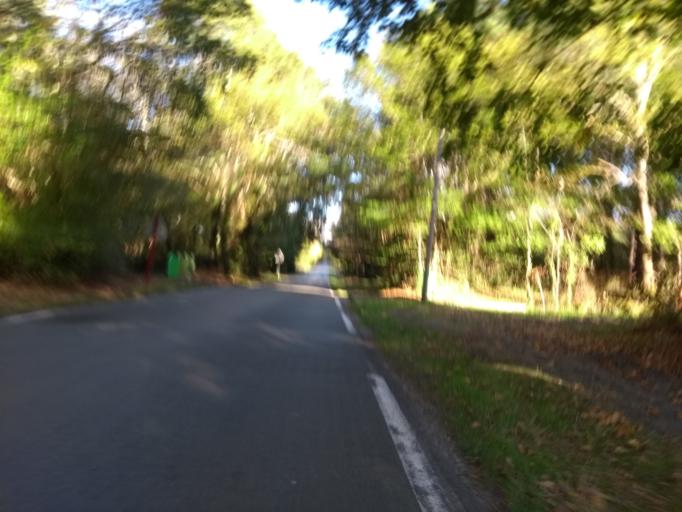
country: FR
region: Aquitaine
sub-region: Departement de la Gironde
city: Canejan
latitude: 44.7464
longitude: -0.6340
